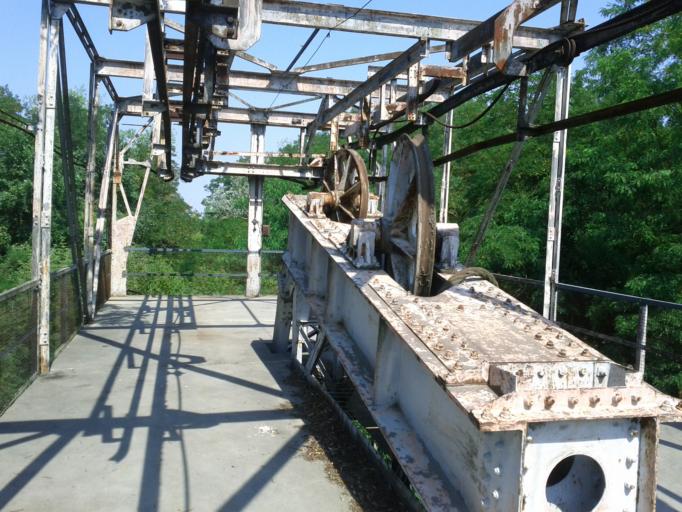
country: DE
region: Brandenburg
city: Woltersdorf
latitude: 52.4816
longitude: 13.7856
